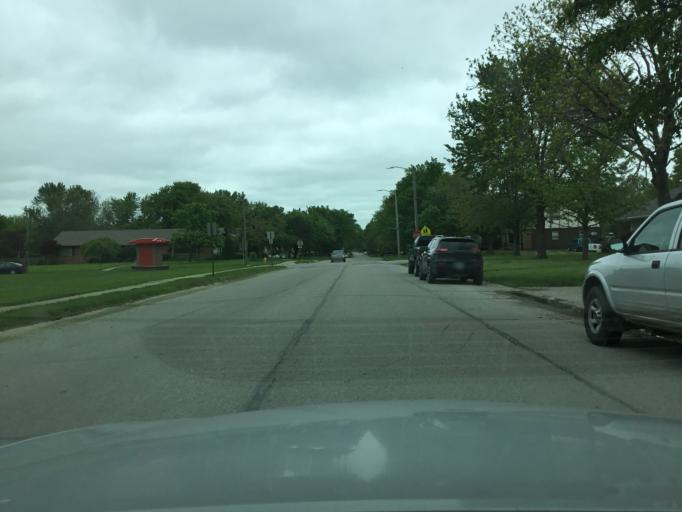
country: US
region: Kansas
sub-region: Franklin County
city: Ottawa
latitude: 38.6006
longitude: -95.2771
